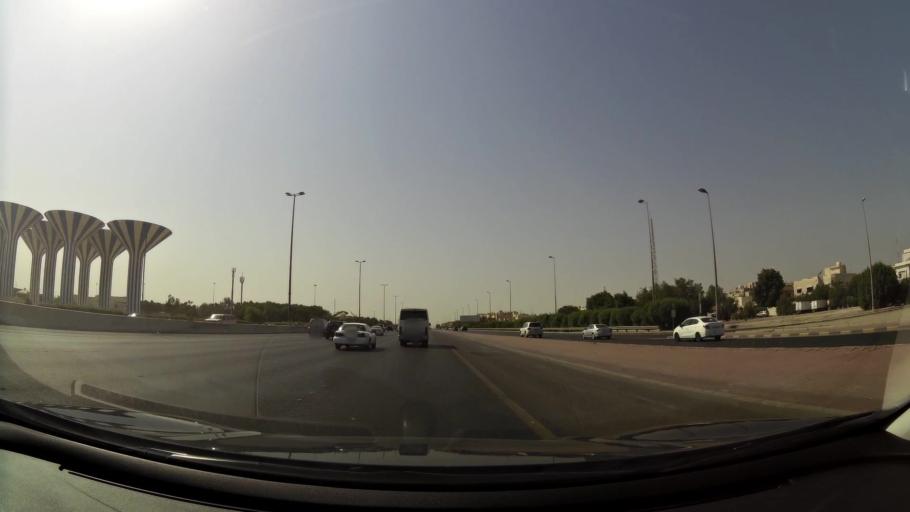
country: KW
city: Bayan
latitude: 29.3104
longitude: 48.0413
